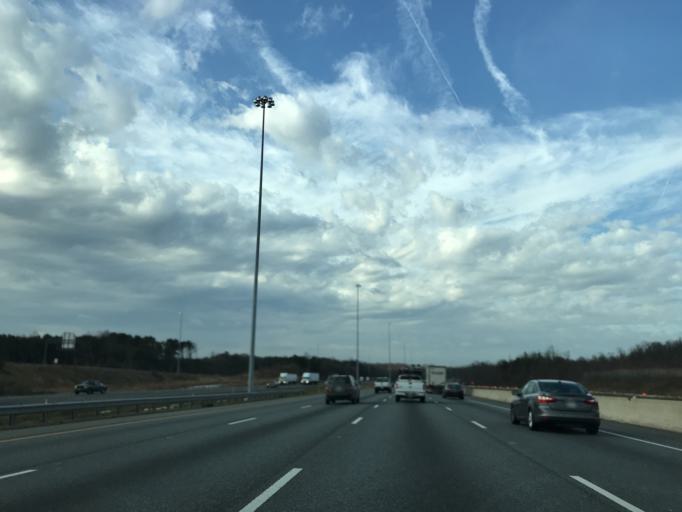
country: US
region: Maryland
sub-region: Prince George's County
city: West Laurel
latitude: 39.0717
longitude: -76.9072
